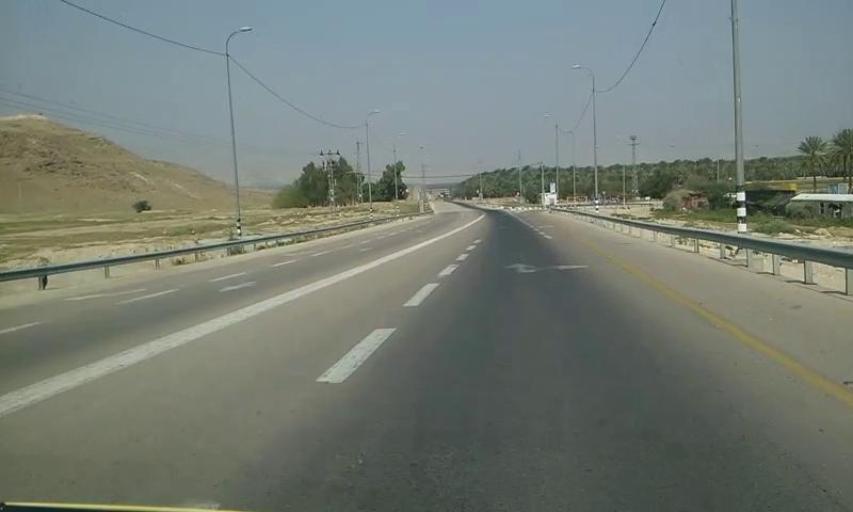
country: PS
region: West Bank
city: Al `Awja
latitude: 31.9760
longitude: 35.4684
